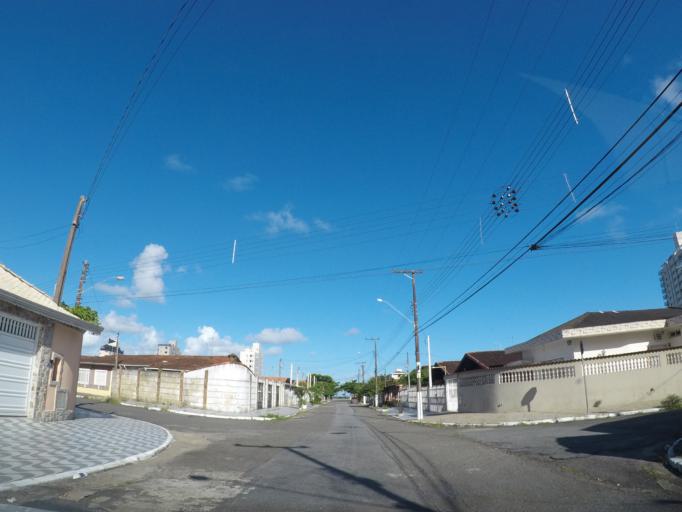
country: BR
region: Sao Paulo
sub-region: Mongagua
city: Mongagua
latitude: -24.0595
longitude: -46.5487
